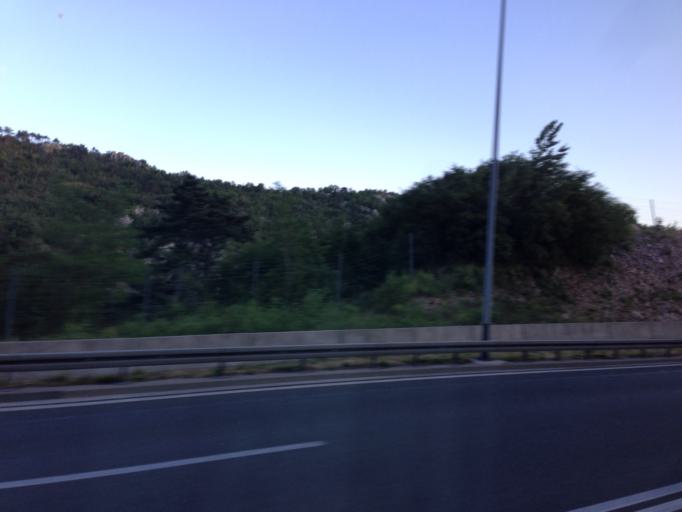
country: HR
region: Primorsko-Goranska
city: Cernik
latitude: 45.3201
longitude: 14.4903
